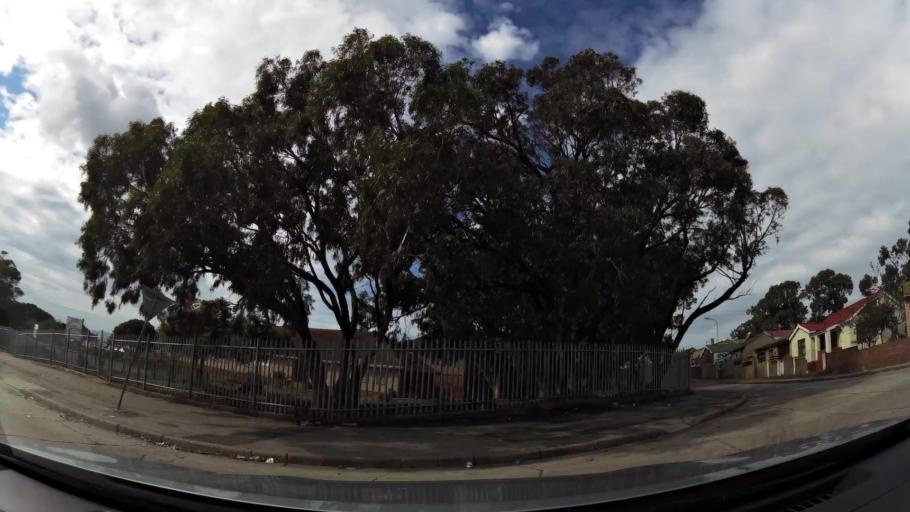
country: ZA
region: Eastern Cape
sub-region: Nelson Mandela Bay Metropolitan Municipality
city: Port Elizabeth
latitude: -33.9295
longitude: 25.5655
